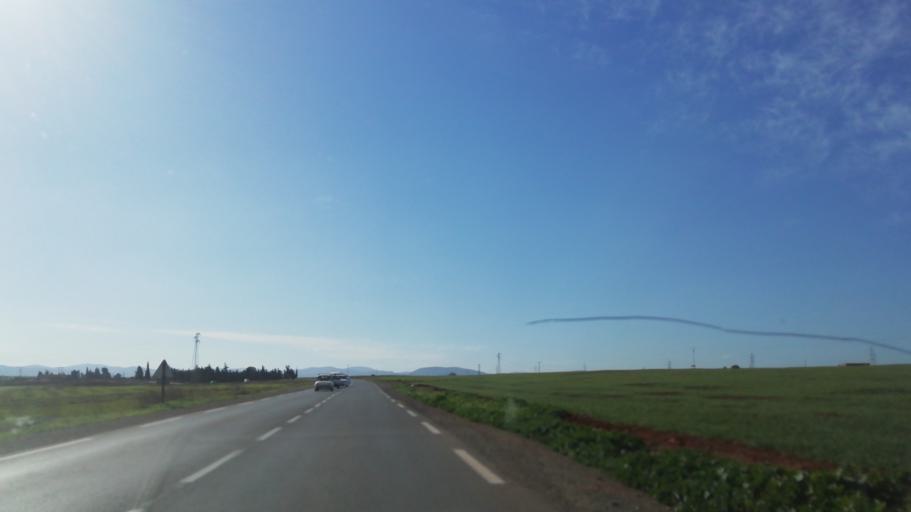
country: DZ
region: Tlemcen
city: Ouled Mimoun
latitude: 34.9967
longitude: -0.9088
